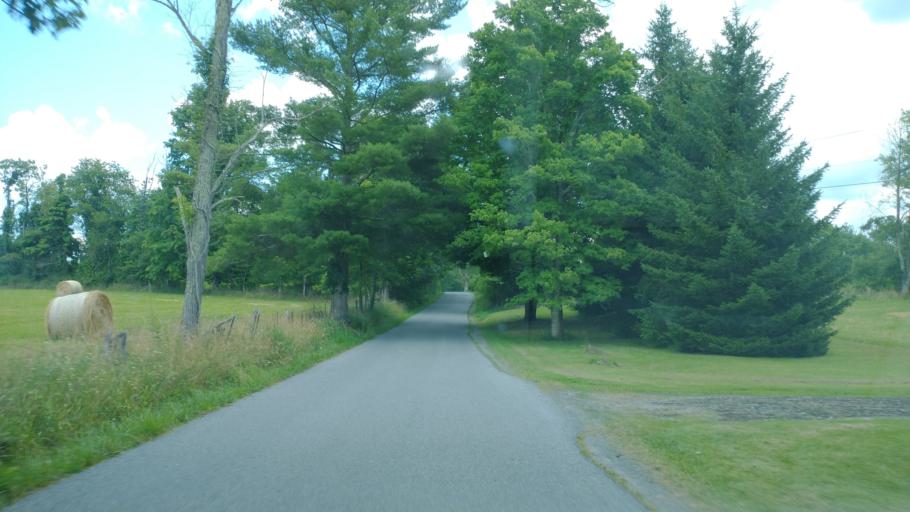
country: US
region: West Virginia
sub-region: Mercer County
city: Athens
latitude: 37.4566
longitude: -81.0328
